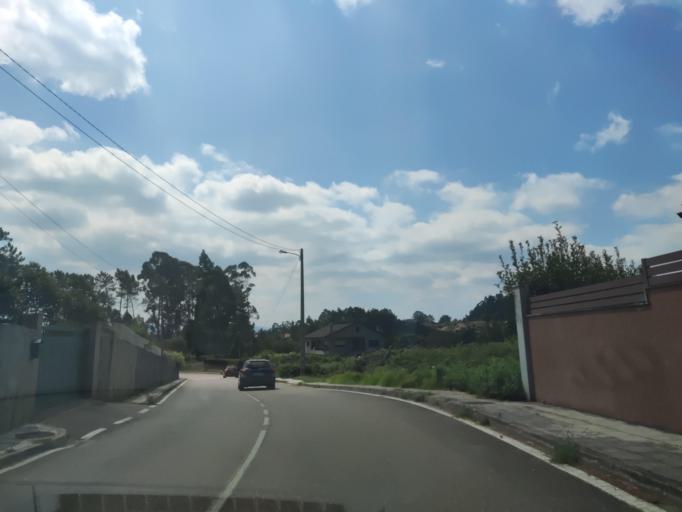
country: ES
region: Galicia
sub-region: Provincia de Pontevedra
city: Porrino
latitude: 42.1475
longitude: -8.6482
